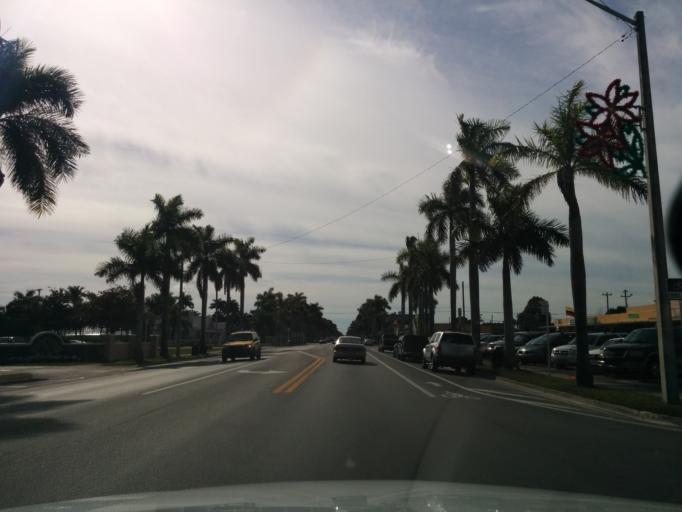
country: US
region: Florida
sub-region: Miami-Dade County
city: Homestead
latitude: 25.4836
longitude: -80.4775
